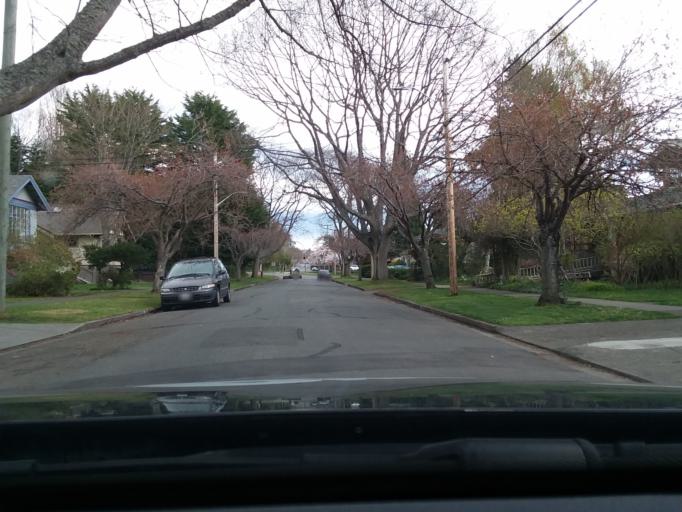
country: CA
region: British Columbia
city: Victoria
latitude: 48.4169
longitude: -123.3467
